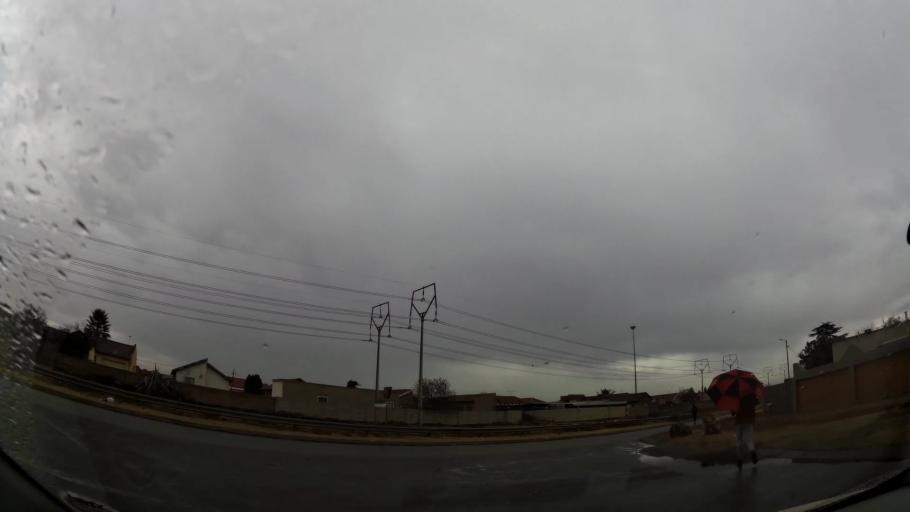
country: ZA
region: Gauteng
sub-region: Ekurhuleni Metropolitan Municipality
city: Germiston
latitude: -26.3371
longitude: 28.2028
